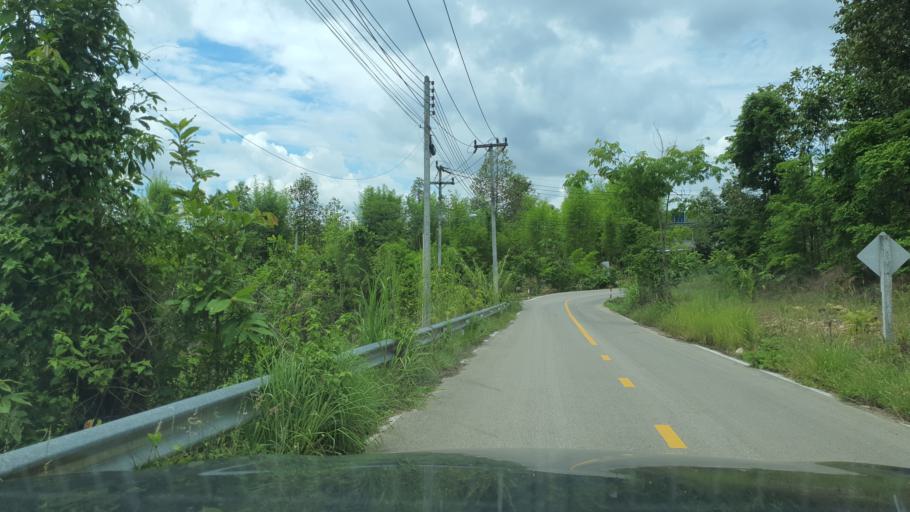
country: TH
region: Chiang Mai
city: San Sai
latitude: 18.9247
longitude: 99.0529
